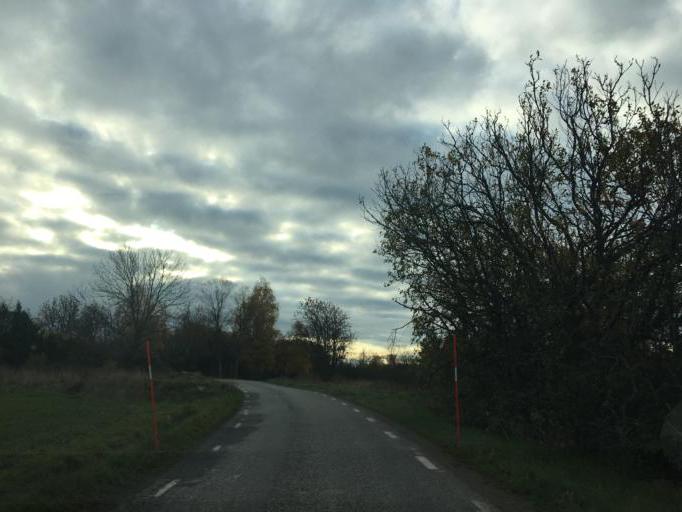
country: SE
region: Vaestmanland
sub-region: Vasteras
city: Vasteras
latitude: 59.5719
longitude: 16.4537
